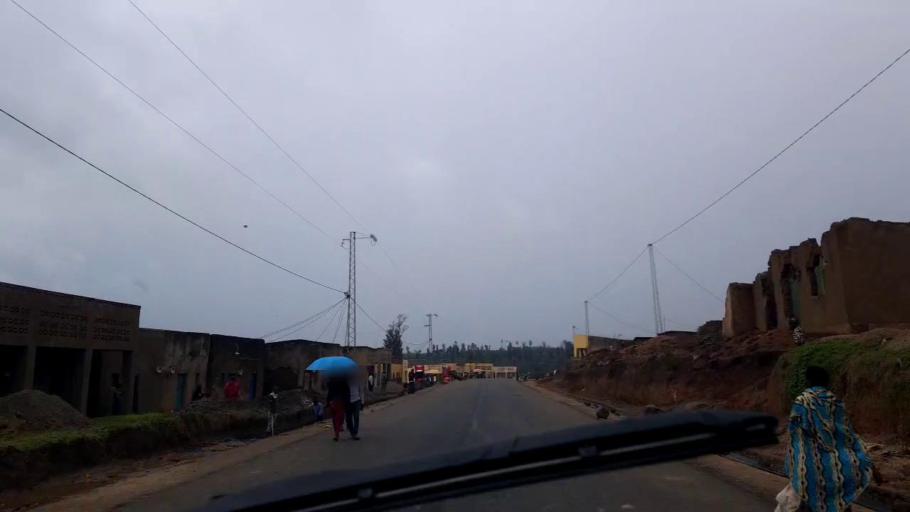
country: RW
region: Northern Province
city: Byumba
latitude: -1.4138
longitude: 30.2821
